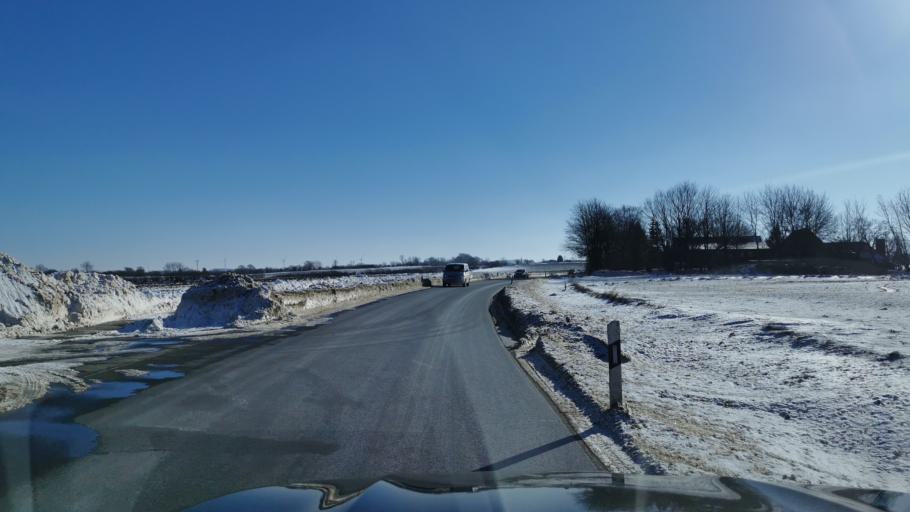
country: DE
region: Schleswig-Holstein
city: Grundhof
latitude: 54.7881
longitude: 9.6435
